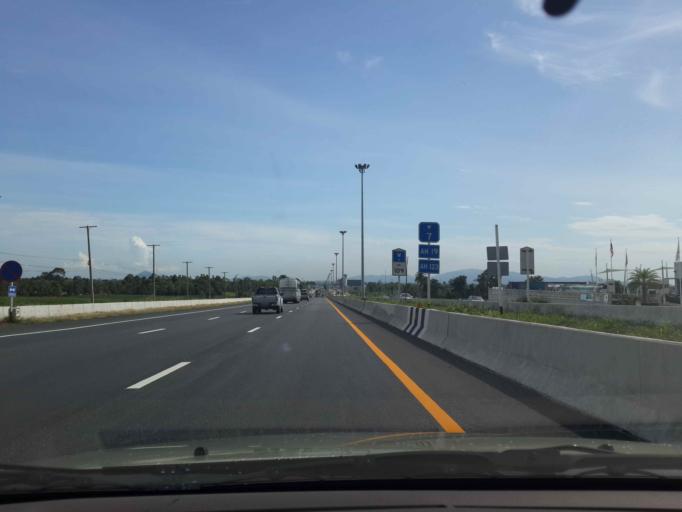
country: TH
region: Chon Buri
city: Ban Talat Bueng
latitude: 13.0345
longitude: 100.9963
